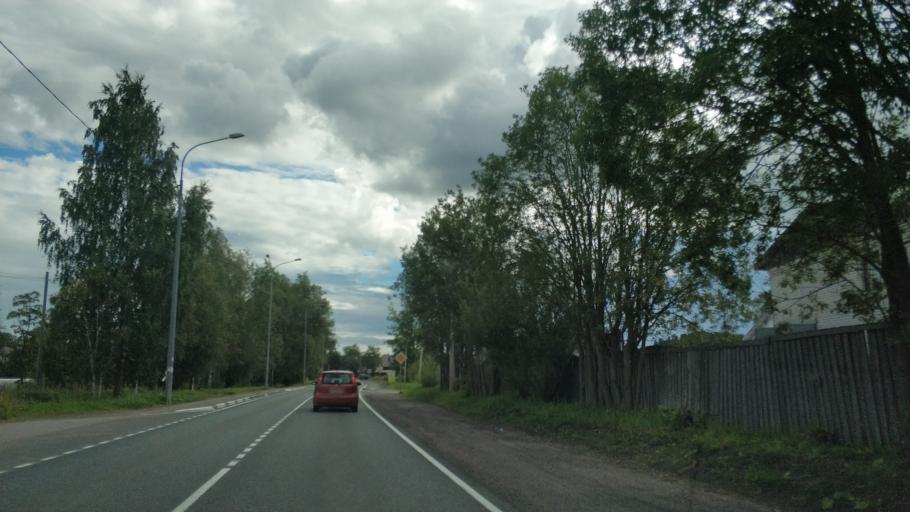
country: RU
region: Republic of Karelia
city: Khelyulya
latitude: 61.7523
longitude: 30.6601
